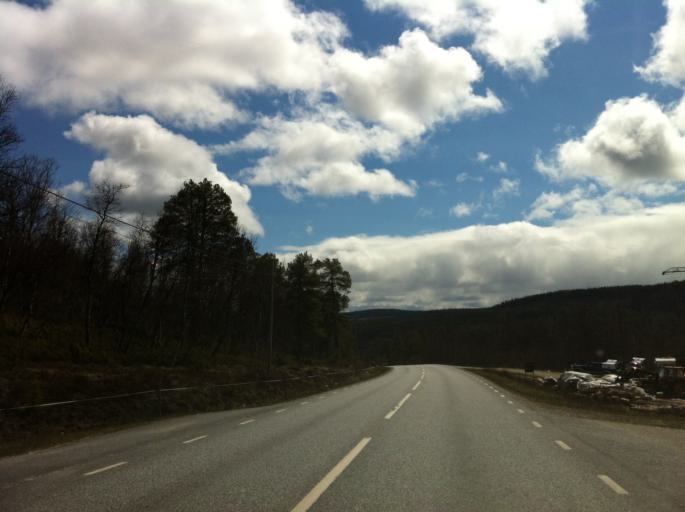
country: NO
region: Sor-Trondelag
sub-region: Tydal
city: Aas
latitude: 62.6283
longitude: 12.4483
